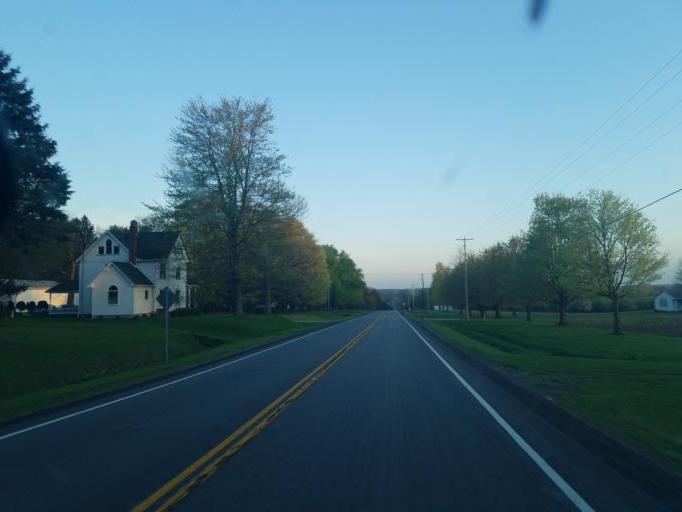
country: US
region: Ohio
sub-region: Trumbull County
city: Brookfield Center
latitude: 41.2858
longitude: -80.5686
